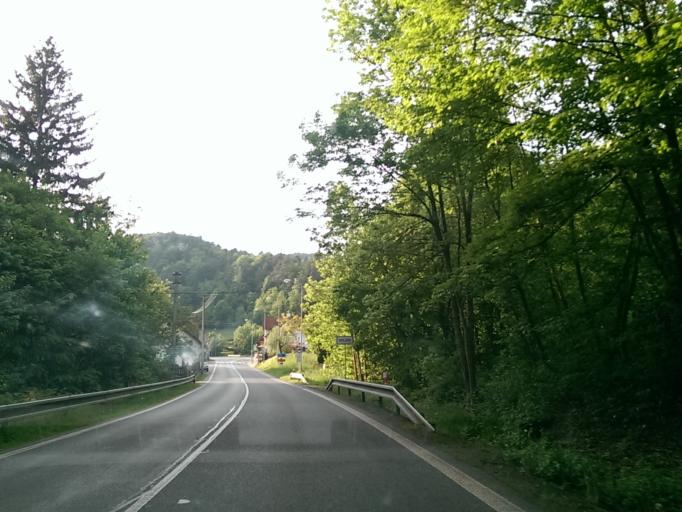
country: CZ
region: Liberecky
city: Mala Skala
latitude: 50.6524
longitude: 15.2212
